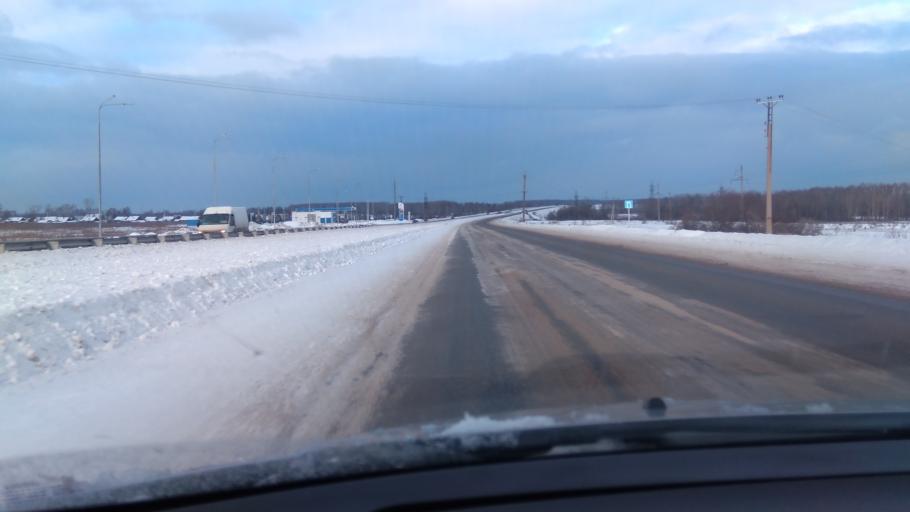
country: RU
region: Sverdlovsk
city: Tsementnyy
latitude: 57.4951
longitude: 60.1759
